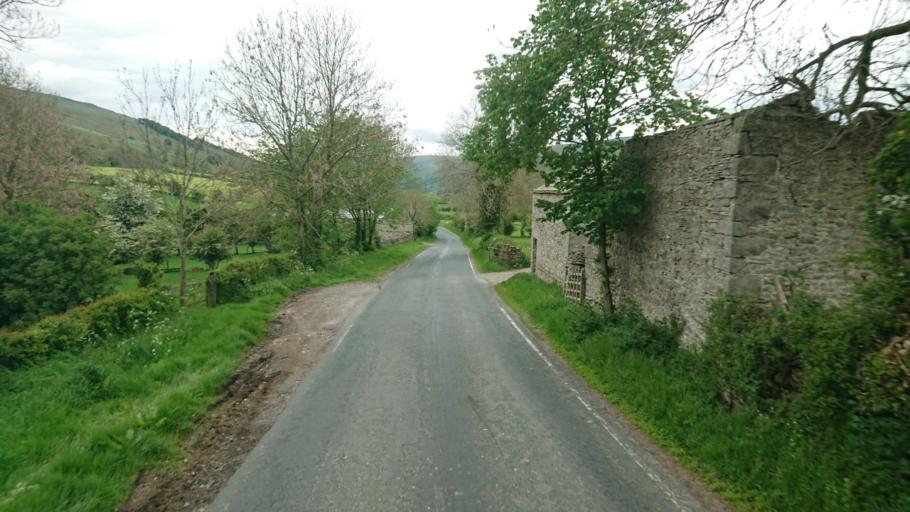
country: GB
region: England
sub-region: North Yorkshire
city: Leyburn
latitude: 54.2685
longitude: -2.0073
